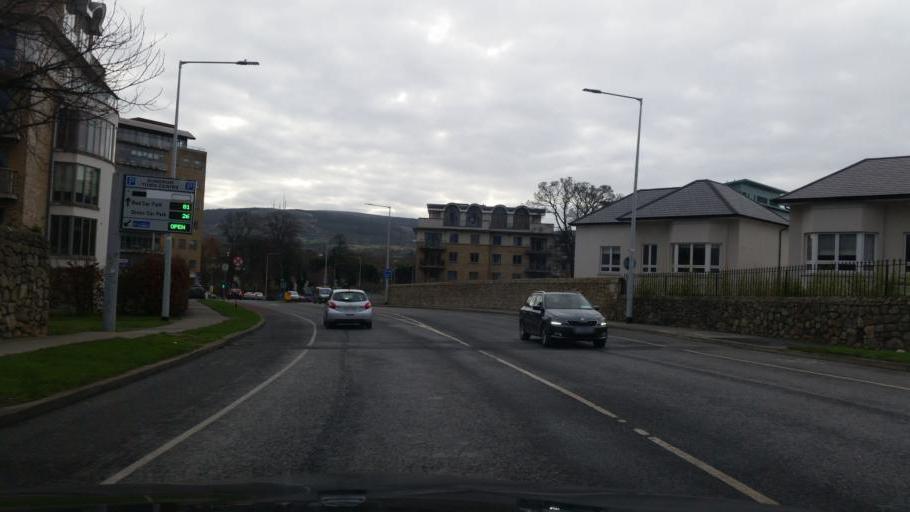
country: IE
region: Leinster
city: Balally
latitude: 53.2876
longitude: -6.2375
